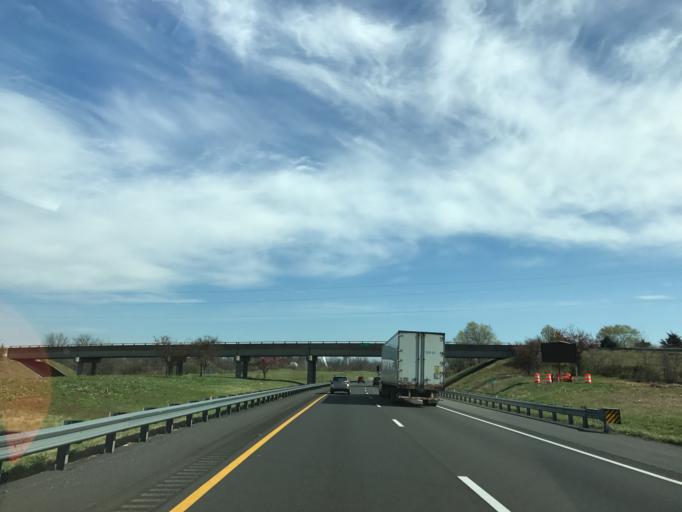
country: US
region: Virginia
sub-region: Shenandoah County
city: Mount Jackson
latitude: 38.7227
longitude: -78.6594
